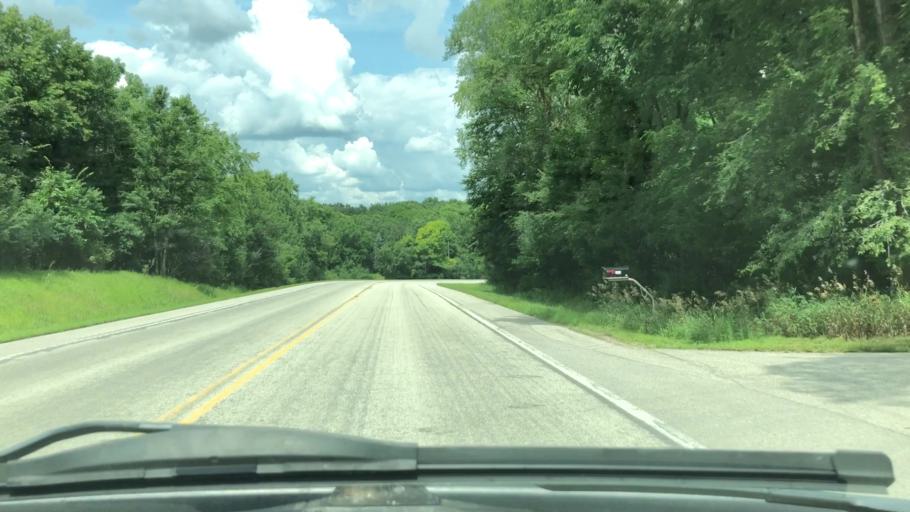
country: US
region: Minnesota
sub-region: Olmsted County
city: Rochester
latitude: 43.9696
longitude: -92.5183
